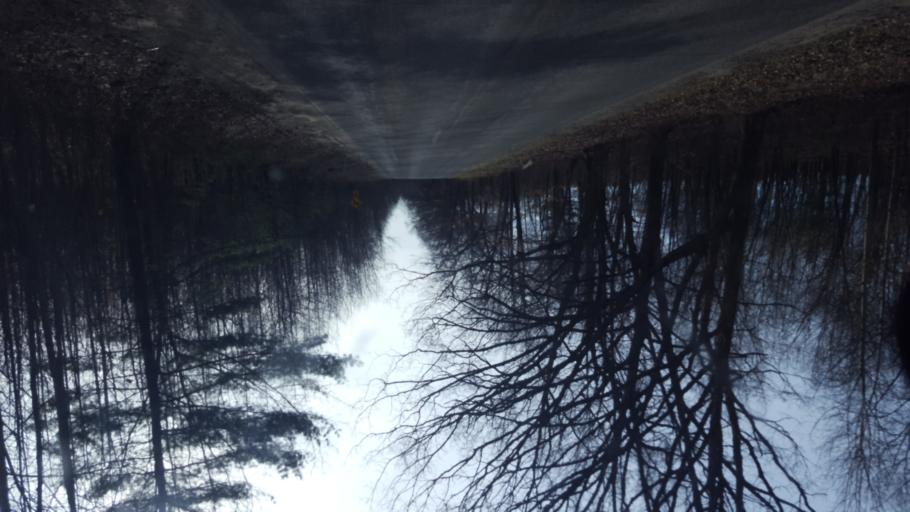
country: US
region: Michigan
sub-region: Mecosta County
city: Big Rapids
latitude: 43.5475
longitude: -85.5406
